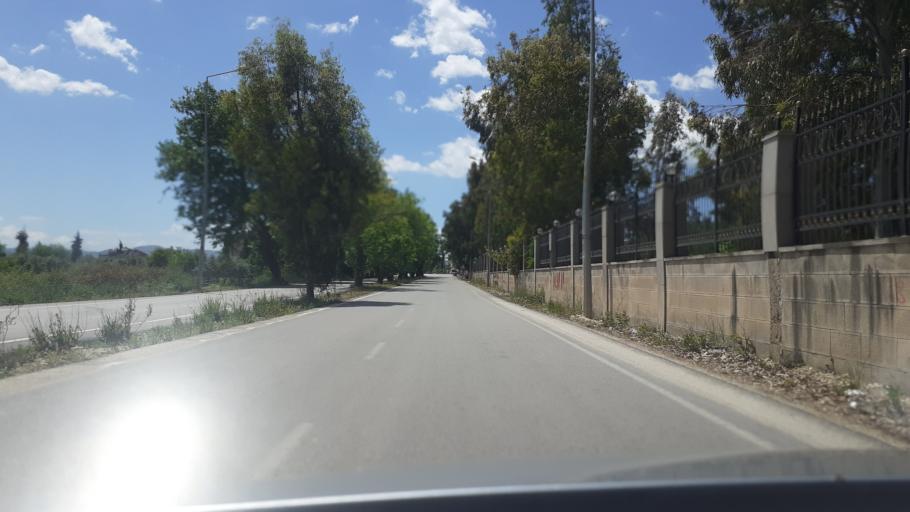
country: TR
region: Hatay
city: Anayazi
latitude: 36.3237
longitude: 36.1981
